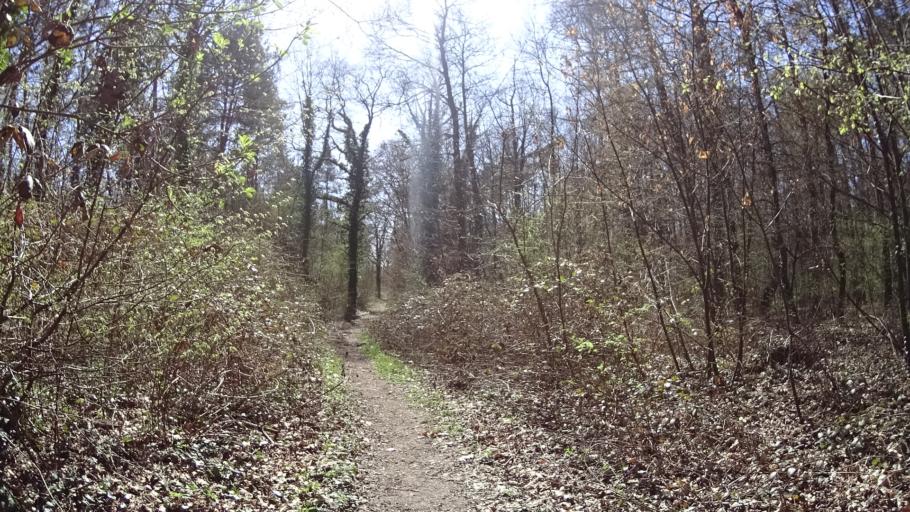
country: DE
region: Baden-Wuerttemberg
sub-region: Karlsruhe Region
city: Plankstadt
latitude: 49.4205
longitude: 8.5760
